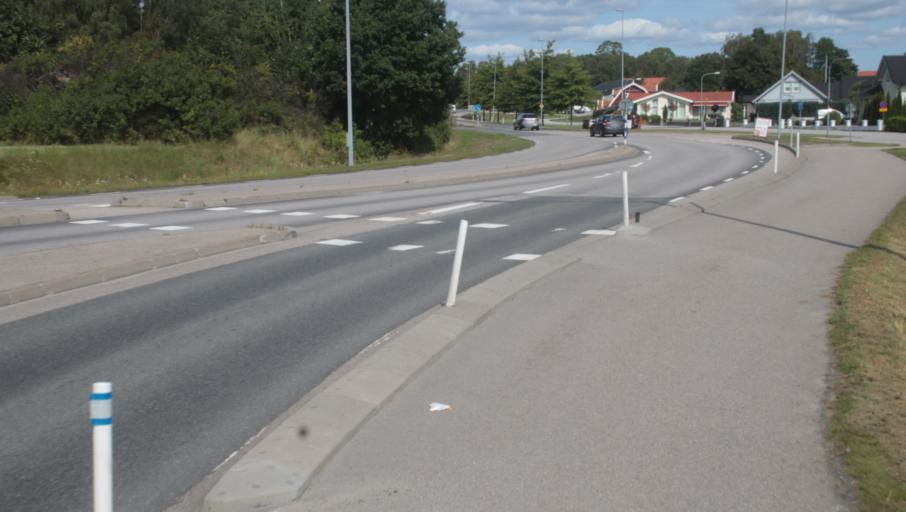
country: SE
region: Blekinge
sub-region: Karlshamns Kommun
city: Karlshamn
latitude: 56.1967
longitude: 14.8396
